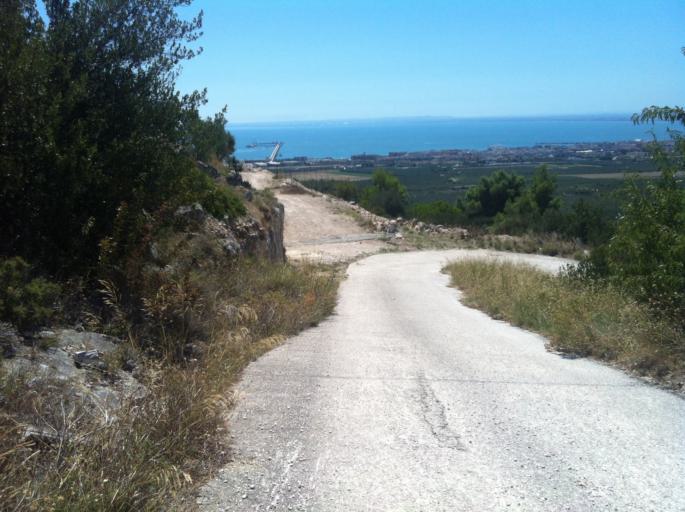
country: IT
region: Apulia
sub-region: Provincia di Foggia
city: Manfredonia
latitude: 41.6633
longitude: 15.9179
